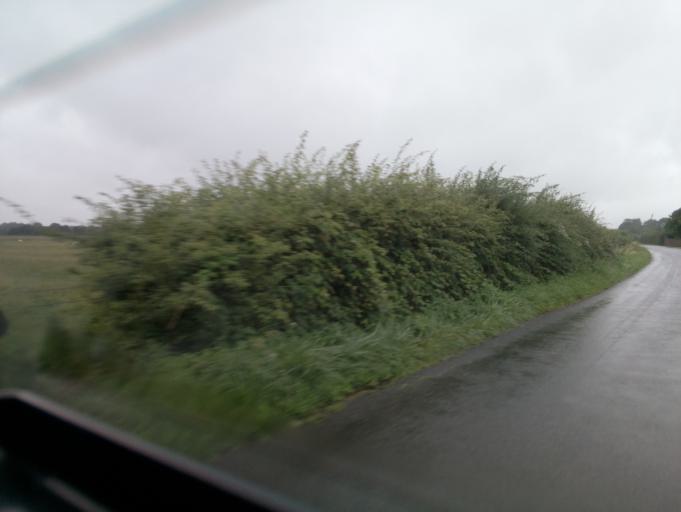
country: GB
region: England
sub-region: Gloucestershire
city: Uckington
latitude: 51.9359
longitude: -2.1239
